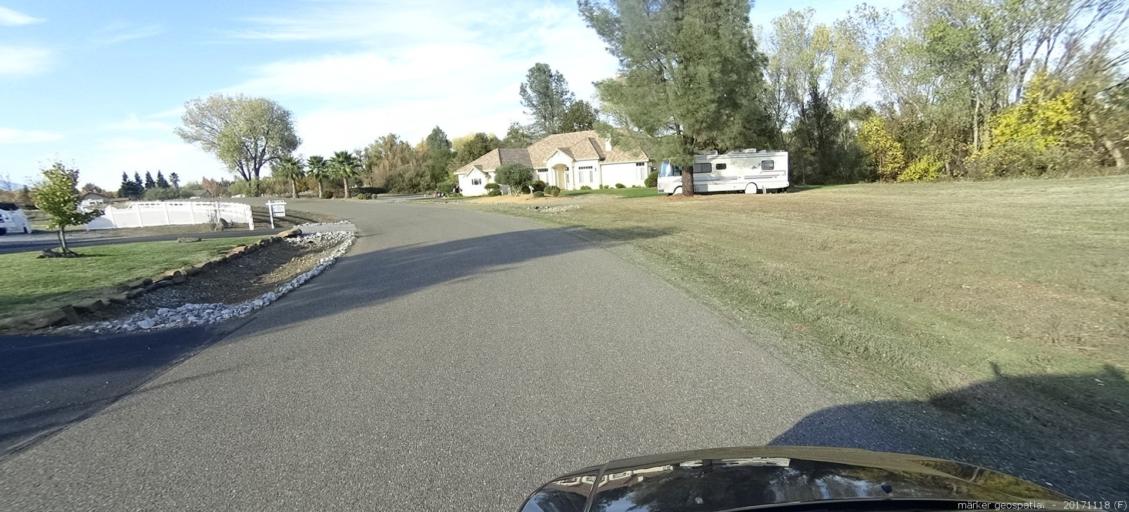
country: US
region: California
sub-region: Shasta County
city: Cottonwood
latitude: 40.3768
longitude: -122.3328
